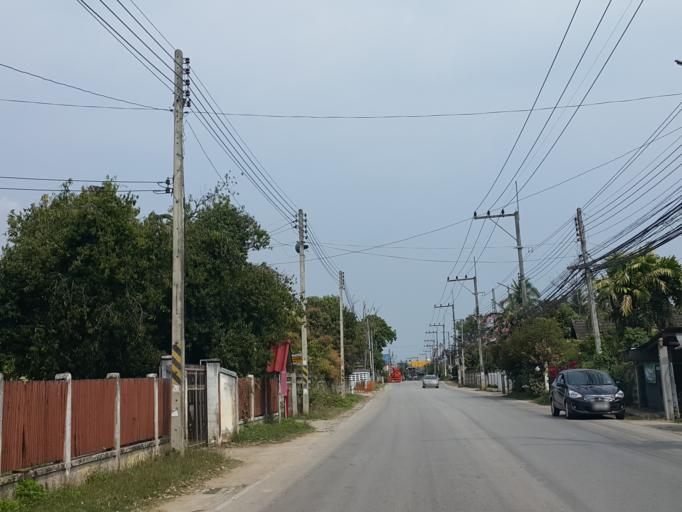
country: TH
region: Lampang
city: Ko Kha
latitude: 18.1855
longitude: 99.3942
